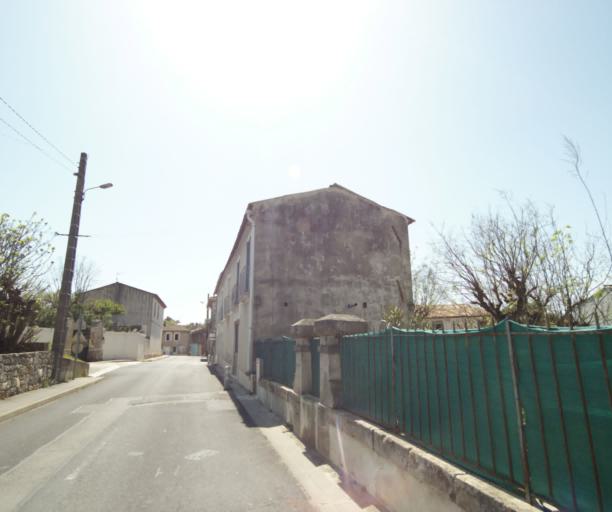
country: FR
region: Languedoc-Roussillon
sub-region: Departement de l'Herault
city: Montferrier-sur-Lez
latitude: 43.6669
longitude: 3.8585
